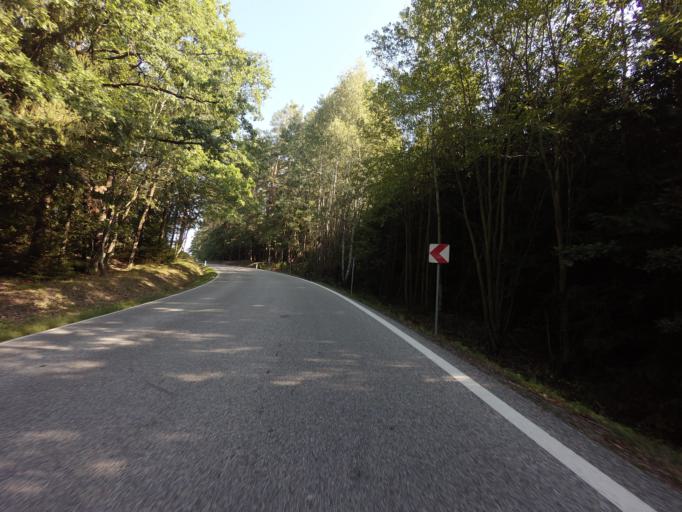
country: CZ
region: Jihocesky
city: Tyn nad Vltavou
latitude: 49.2643
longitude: 14.4121
